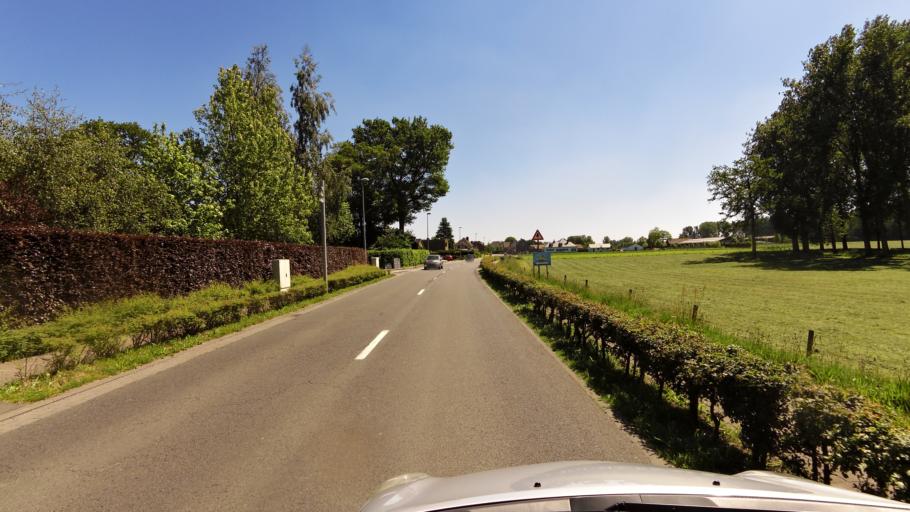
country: BE
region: Flanders
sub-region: Provincie West-Vlaanderen
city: Oostkamp
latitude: 51.1391
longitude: 3.2511
